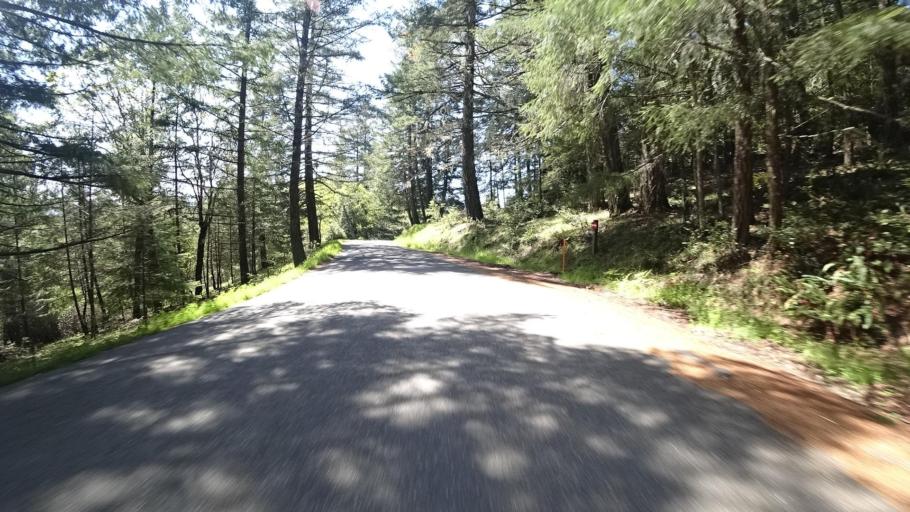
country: US
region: California
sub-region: Humboldt County
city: Redway
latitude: 40.0367
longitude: -123.6394
